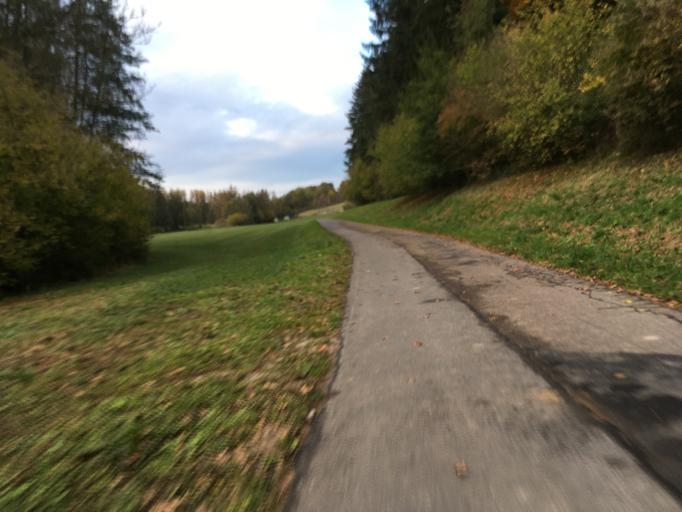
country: DE
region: Baden-Wuerttemberg
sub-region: Karlsruhe Region
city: Rosenberg
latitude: 49.3844
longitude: 9.5003
